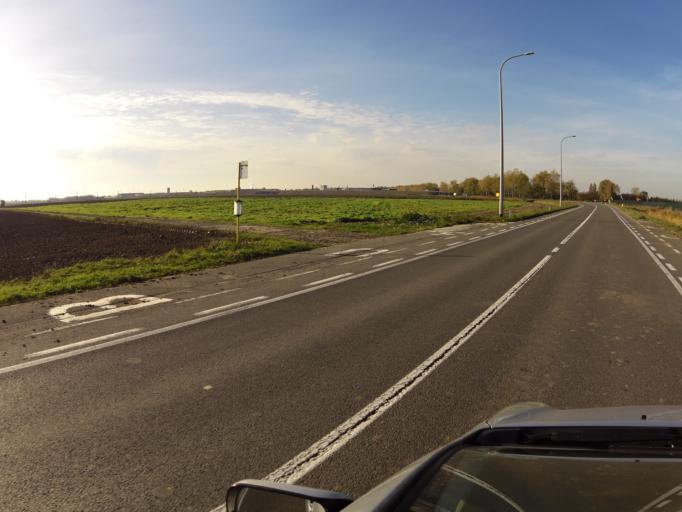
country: BE
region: Flanders
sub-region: Provincie West-Vlaanderen
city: Veurne
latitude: 51.0701
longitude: 2.7097
